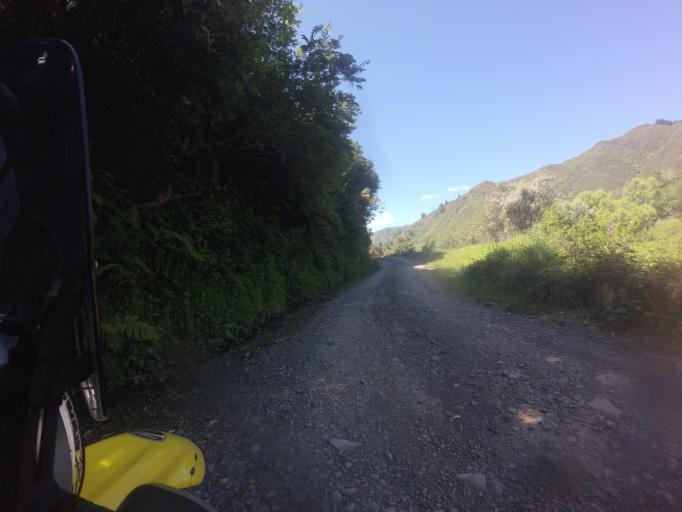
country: NZ
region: Bay of Plenty
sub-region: Opotiki District
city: Opotiki
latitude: -38.3035
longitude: 177.3310
